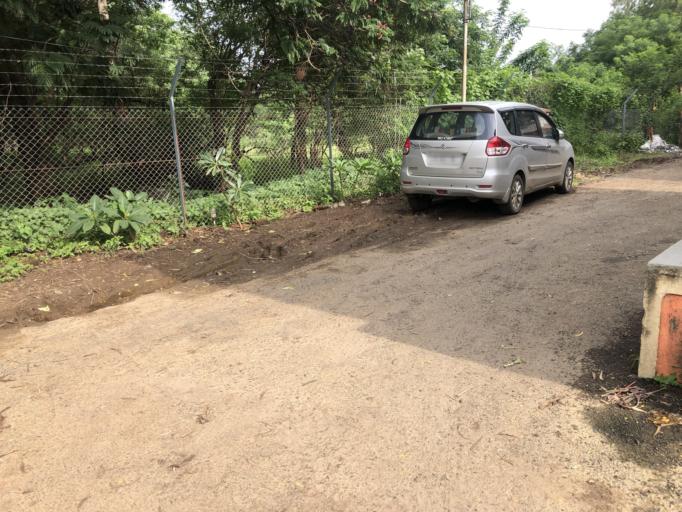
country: IN
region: Maharashtra
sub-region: Pune Division
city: Pimpri
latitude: 18.5907
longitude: 73.7853
